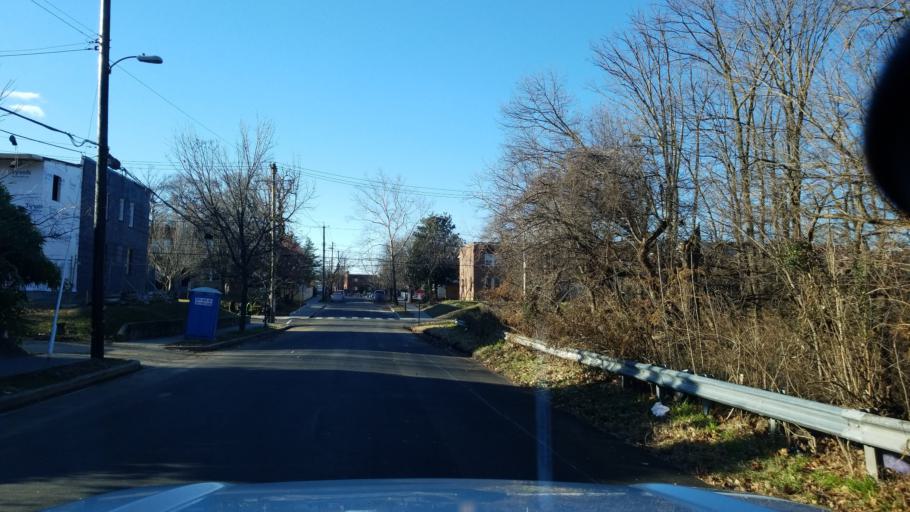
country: US
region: Maryland
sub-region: Prince George's County
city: Glassmanor
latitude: 38.8485
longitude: -77.0024
